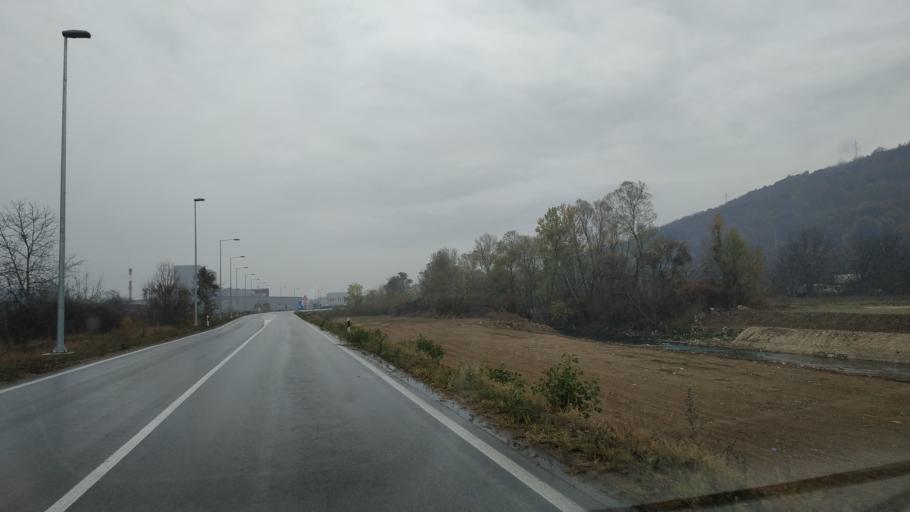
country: RS
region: Central Serbia
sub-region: Pirotski Okrug
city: Pirot
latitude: 43.1805
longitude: 22.5695
